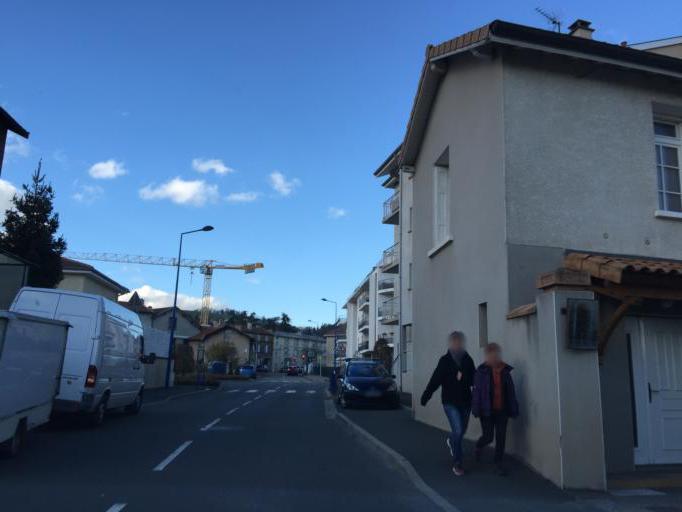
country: FR
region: Rhone-Alpes
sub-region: Departement de la Loire
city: La Talaudiere
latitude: 45.4835
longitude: 4.4373
